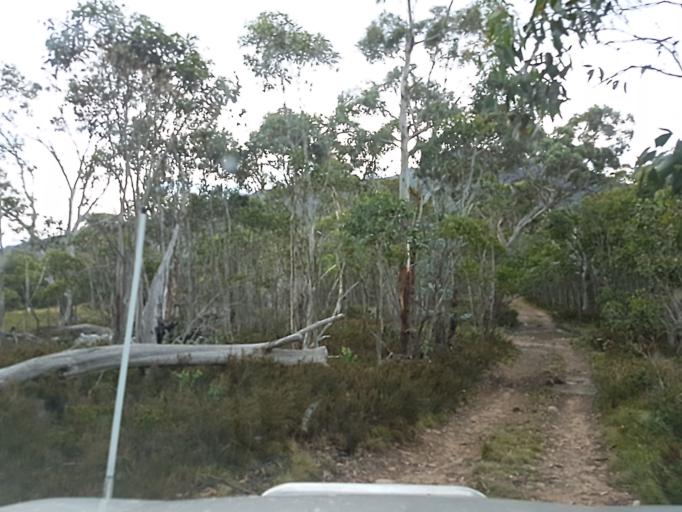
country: AU
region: New South Wales
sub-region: Snowy River
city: Jindabyne
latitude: -36.8801
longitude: 148.1597
